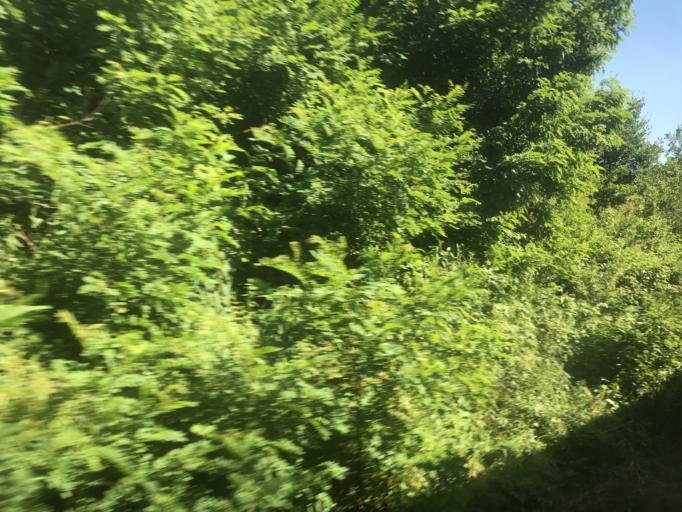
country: AT
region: Upper Austria
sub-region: Politischer Bezirk Freistadt
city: Freistadt
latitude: 48.4902
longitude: 14.4915
